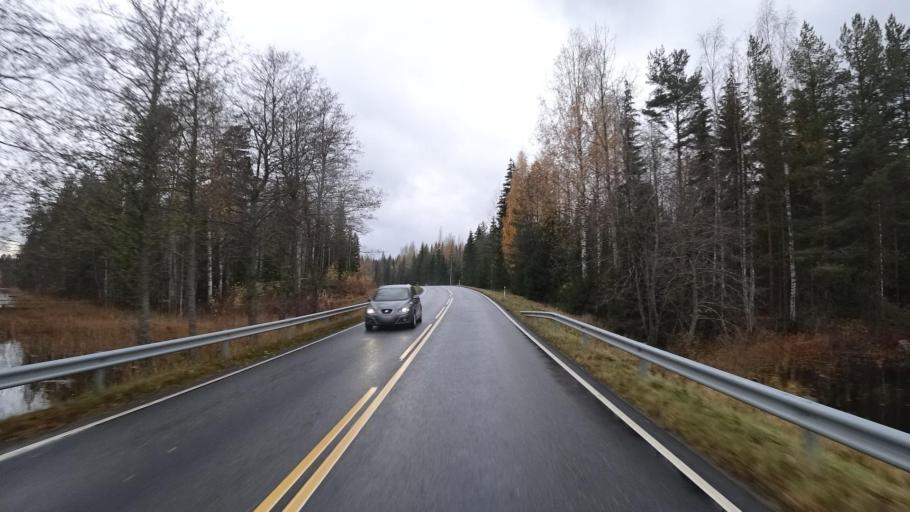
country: FI
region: Southern Savonia
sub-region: Mikkeli
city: Kangasniemi
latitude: 62.1416
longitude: 26.7921
